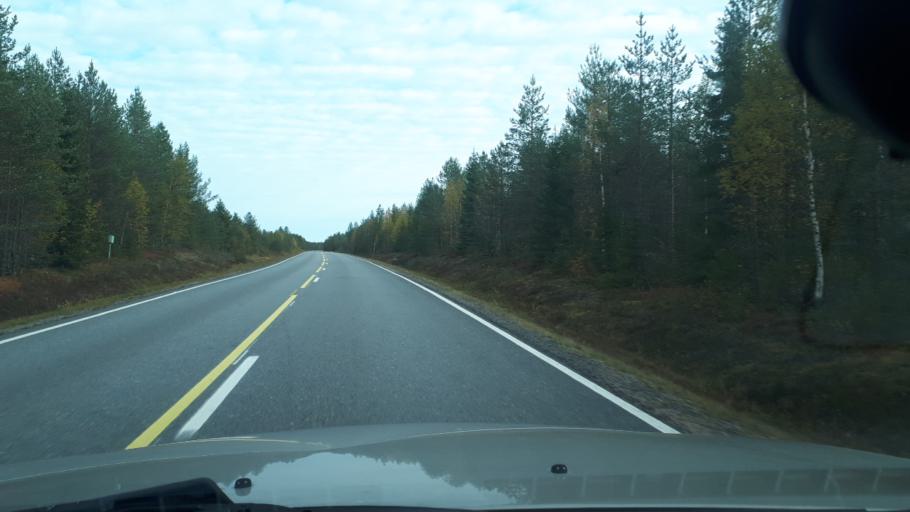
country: FI
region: Northern Ostrobothnia
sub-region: Oulu
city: Yli-Ii
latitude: 65.9028
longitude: 25.7340
